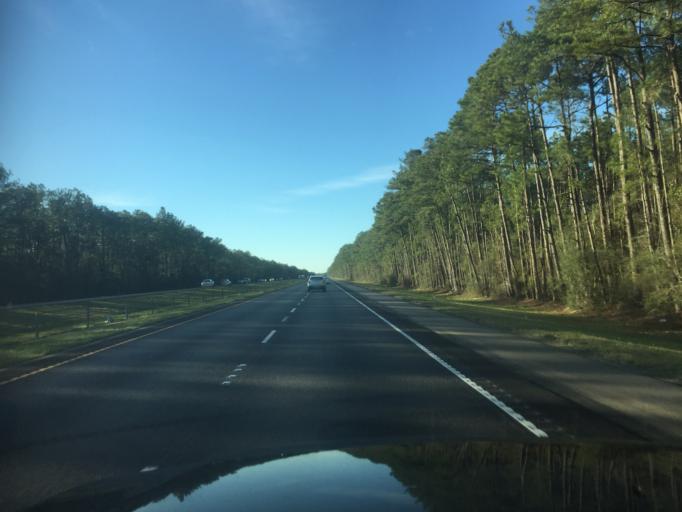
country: US
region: Louisiana
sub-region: Saint Tammany Parish
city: Lacombe
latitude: 30.3619
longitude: -89.9385
